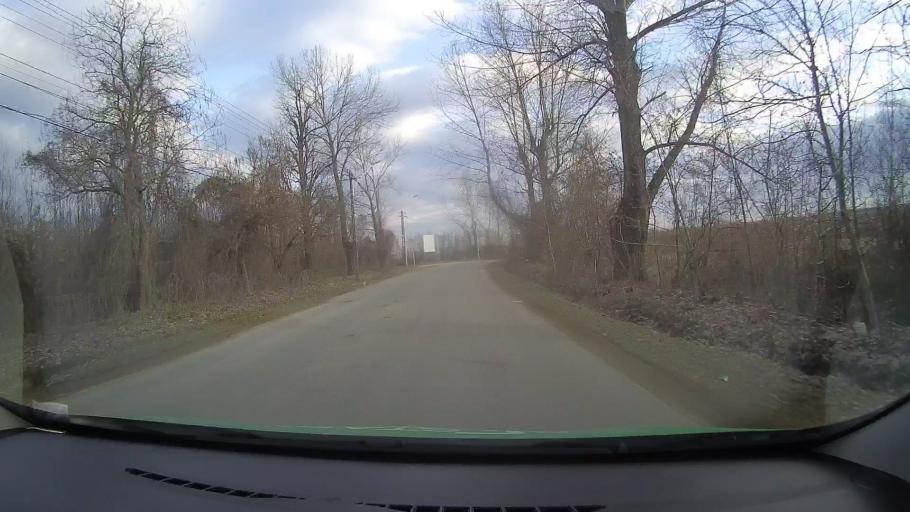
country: RO
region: Dambovita
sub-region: Municipiul Moreni
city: Moreni
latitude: 44.9626
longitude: 25.6566
